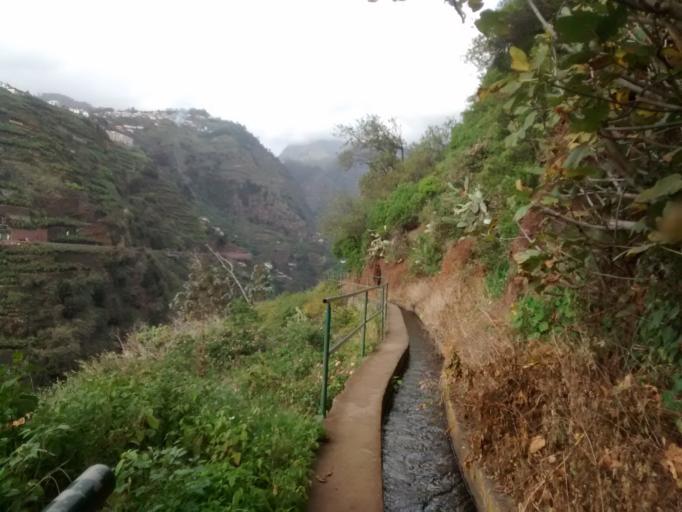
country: PT
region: Madeira
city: Camara de Lobos
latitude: 32.6572
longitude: -16.9610
